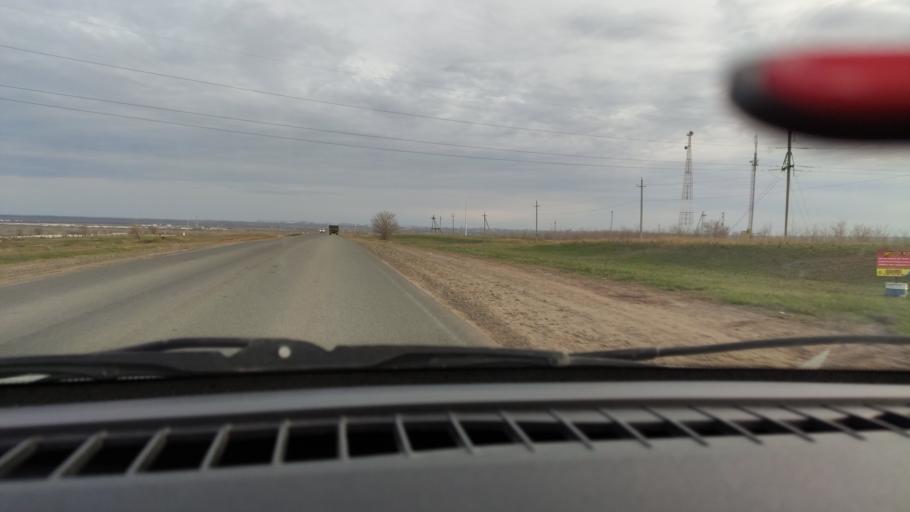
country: RU
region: Orenburg
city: Tatarskaya Kargala
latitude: 51.9575
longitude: 55.1835
